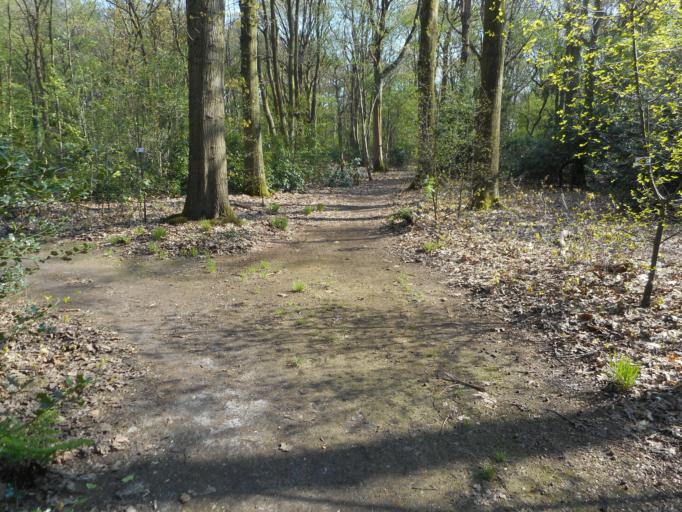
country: BE
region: Flanders
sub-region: Provincie Antwerpen
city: Zoersel
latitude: 51.2572
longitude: 4.7081
